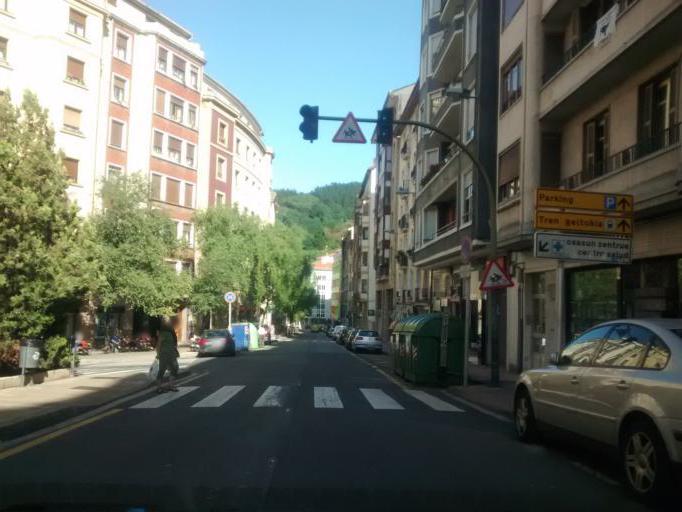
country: ES
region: Basque Country
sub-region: Provincia de Guipuzcoa
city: Eibar
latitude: 43.1852
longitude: -2.4694
